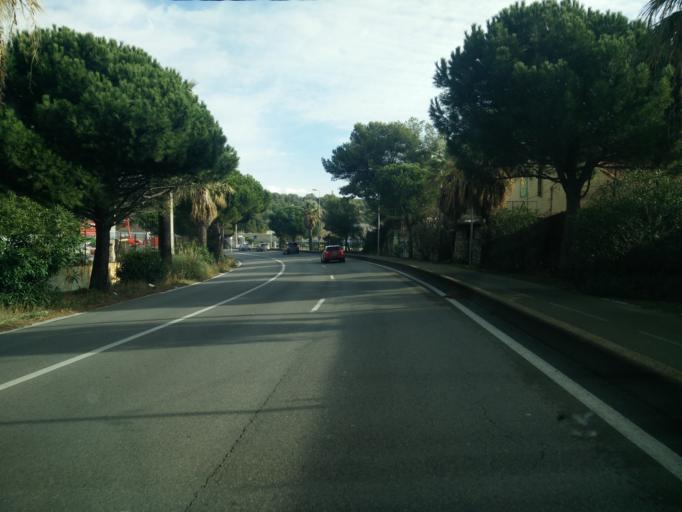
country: FR
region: Provence-Alpes-Cote d'Azur
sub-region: Departement du Var
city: La Seyne-sur-Mer
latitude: 43.1207
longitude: 5.8917
